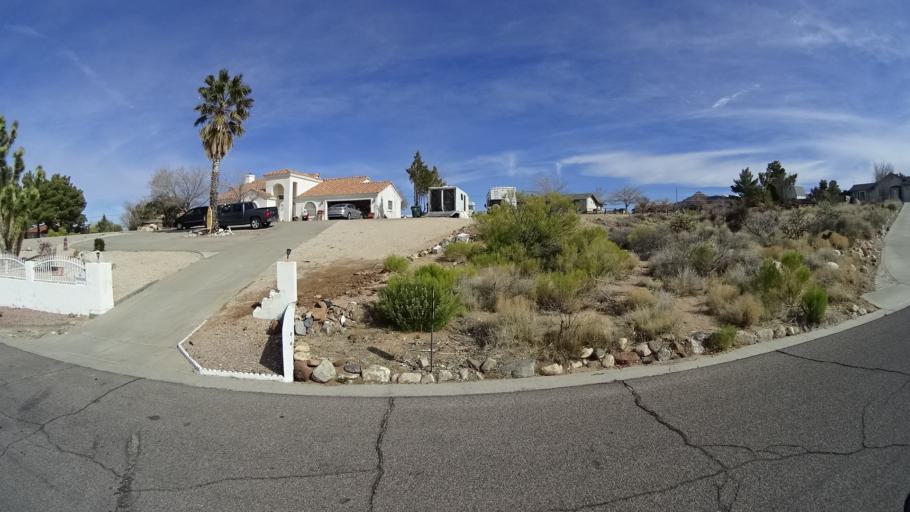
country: US
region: Arizona
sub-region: Mohave County
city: Kingman
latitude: 35.1837
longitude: -113.9862
